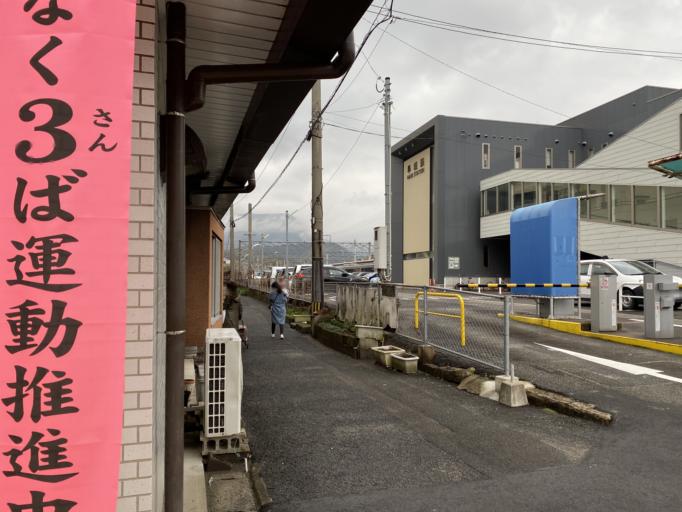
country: JP
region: Nagasaki
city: Sasebo
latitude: 33.1335
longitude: 129.7988
